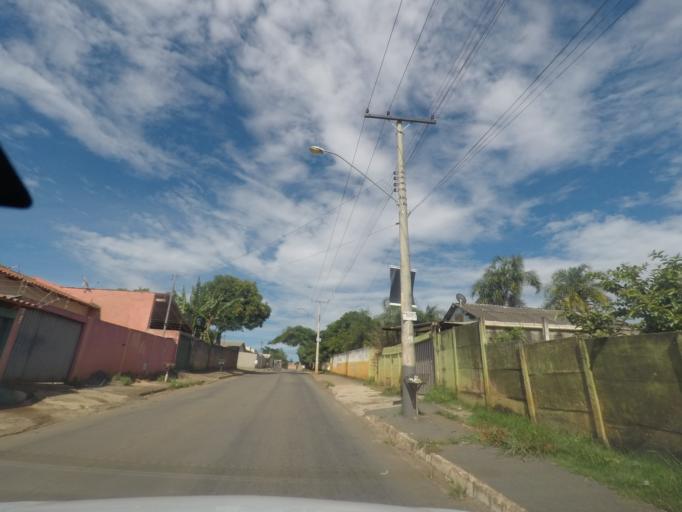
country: BR
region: Goias
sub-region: Aparecida De Goiania
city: Aparecida de Goiania
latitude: -16.7986
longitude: -49.2752
